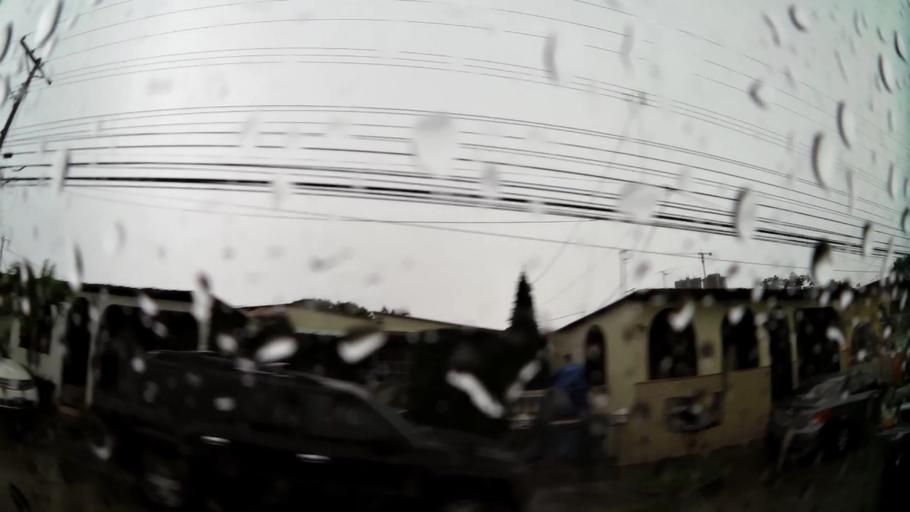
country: PA
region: Panama
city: San Miguelito
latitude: 9.0516
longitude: -79.4745
